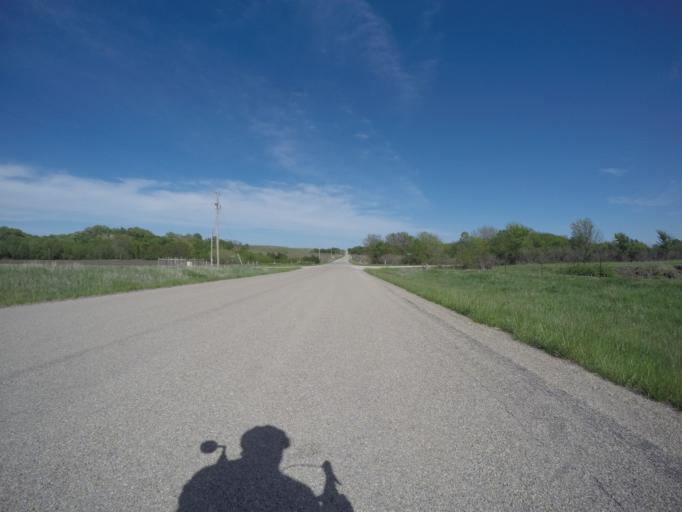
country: US
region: Kansas
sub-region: Riley County
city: Ogden
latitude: 38.9718
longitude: -96.5626
